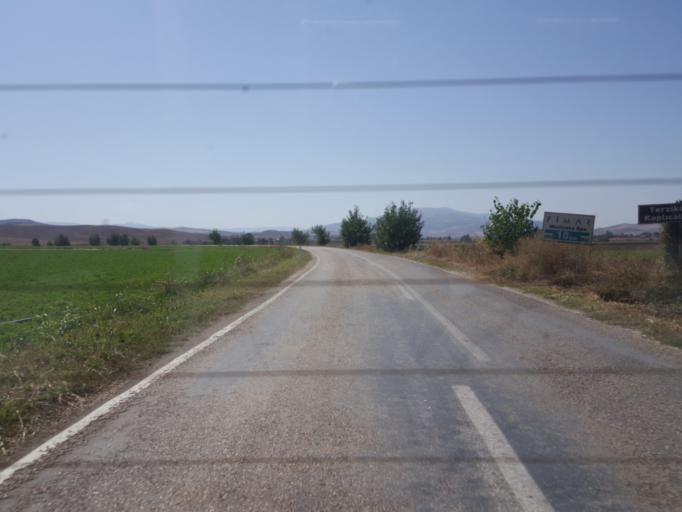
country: TR
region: Amasya
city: Dogantepe
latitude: 40.5291
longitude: 35.6648
